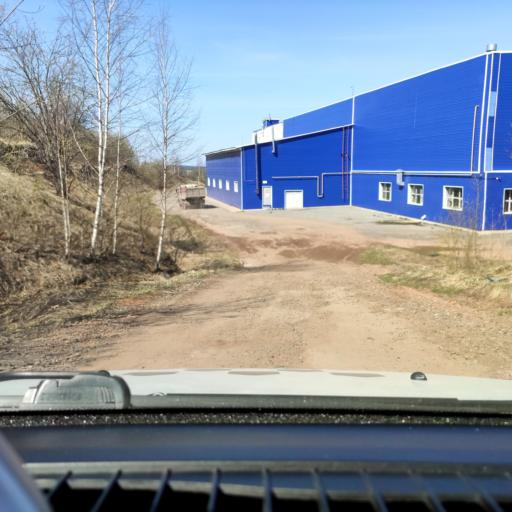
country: RU
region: Perm
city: Perm
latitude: 58.0687
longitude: 56.3726
